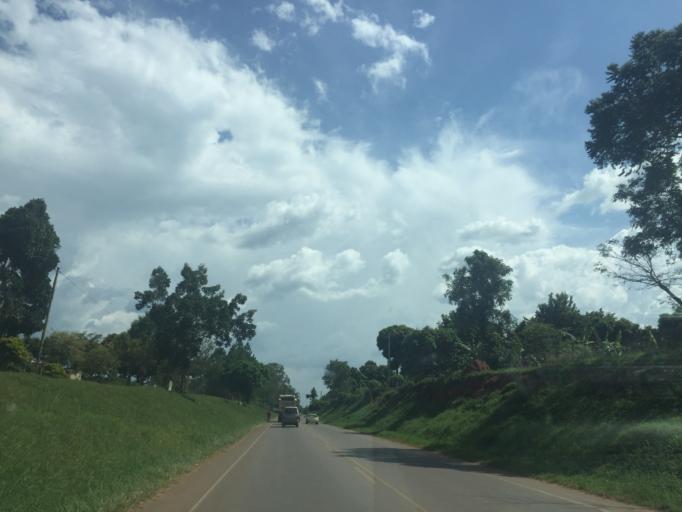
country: UG
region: Central Region
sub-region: Luwero District
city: Wobulenzi
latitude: 0.7571
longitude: 32.5141
